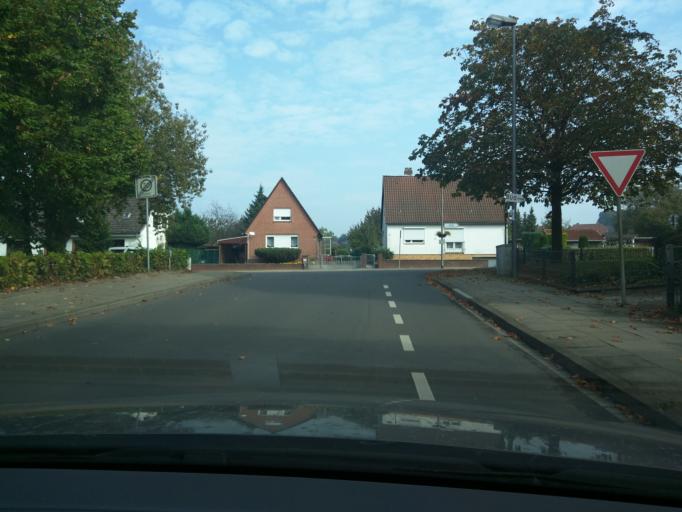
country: DE
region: Schleswig-Holstein
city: Lauenburg
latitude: 53.3771
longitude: 10.5513
